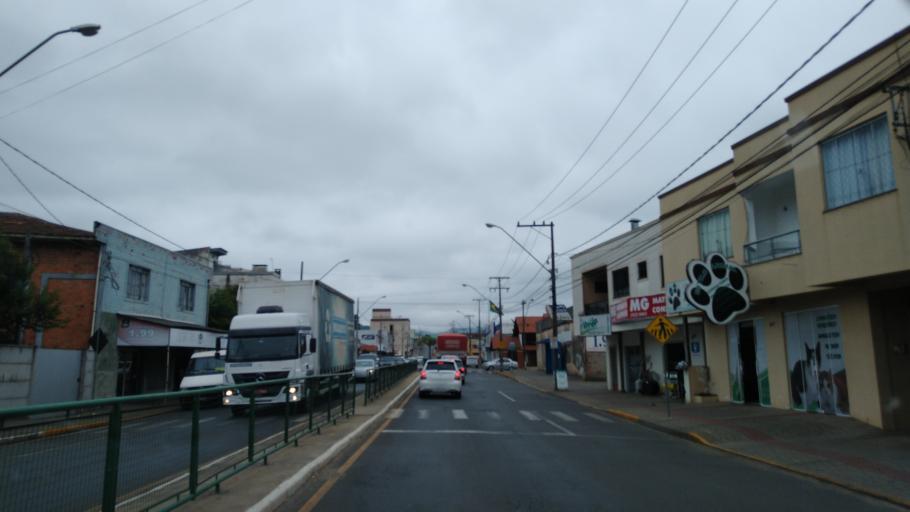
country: BR
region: Santa Catarina
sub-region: Porto Uniao
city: Porto Uniao
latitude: -26.2517
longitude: -51.0856
